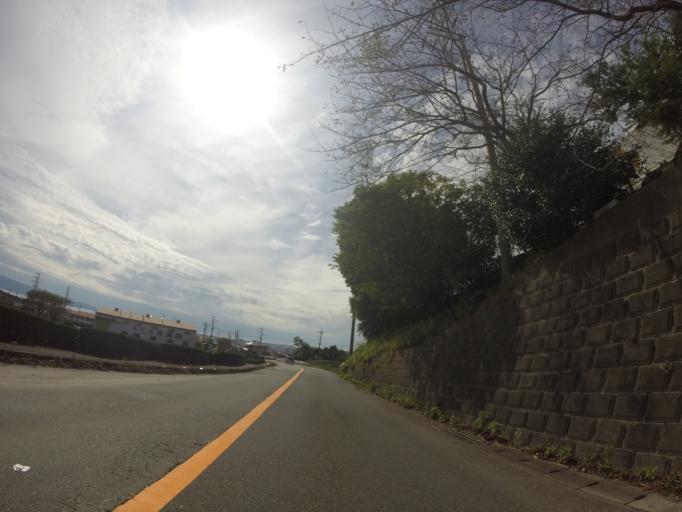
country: JP
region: Shizuoka
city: Fuji
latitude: 35.1911
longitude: 138.6979
